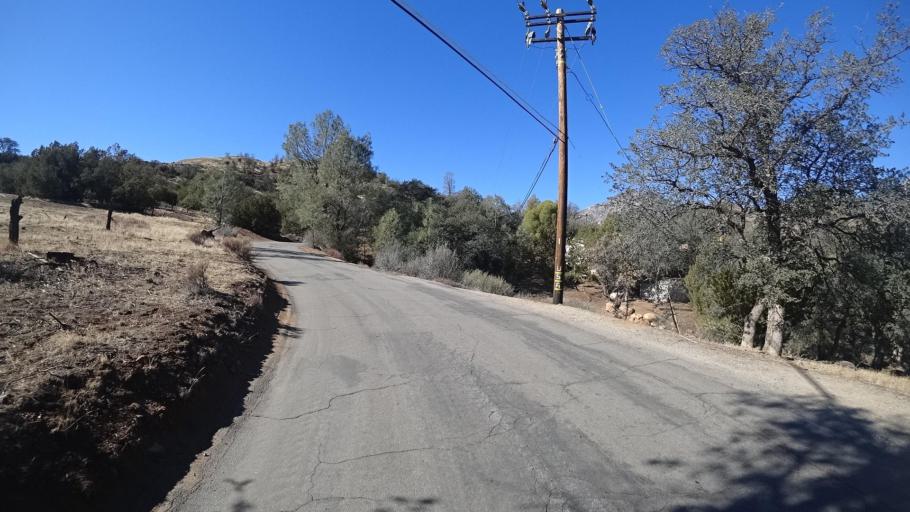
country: US
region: California
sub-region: Kern County
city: Wofford Heights
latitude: 35.7070
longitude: -118.4682
